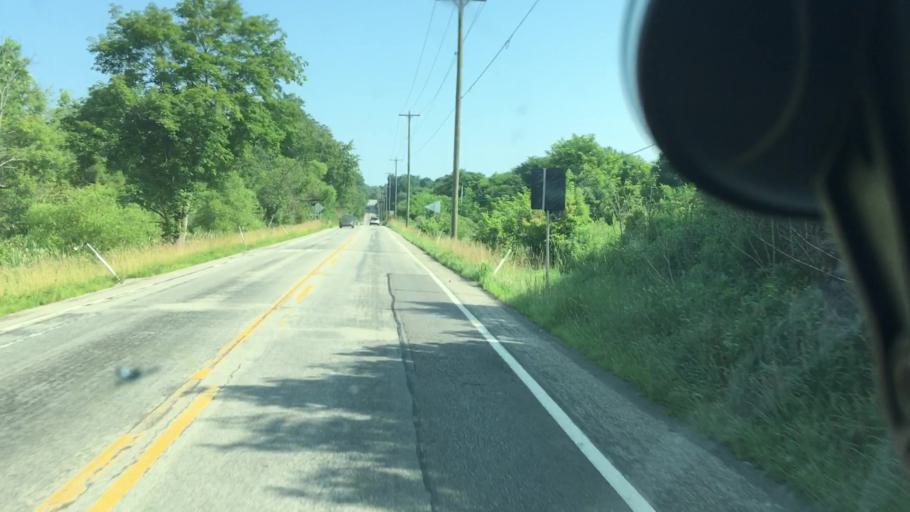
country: US
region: Pennsylvania
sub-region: Lawrence County
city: New Castle
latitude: 40.9920
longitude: -80.2680
